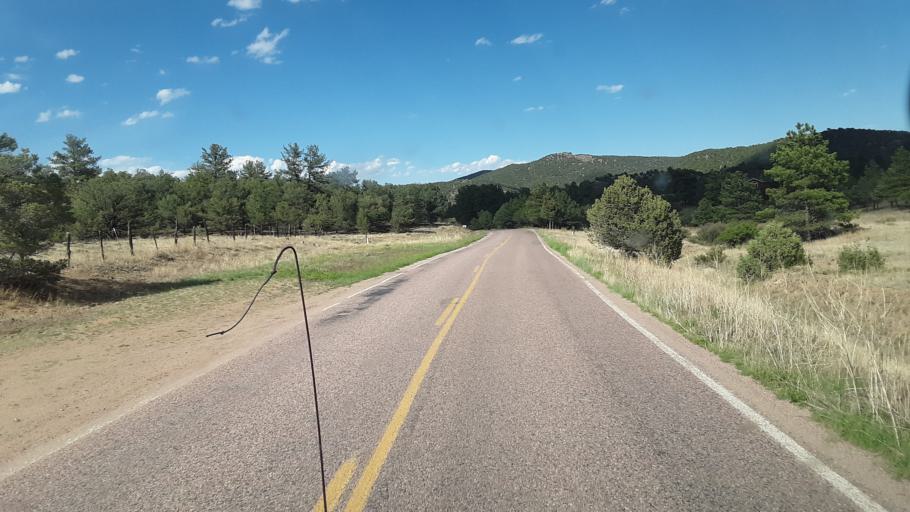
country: US
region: Colorado
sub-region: Custer County
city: Westcliffe
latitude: 38.3613
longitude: -105.4696
